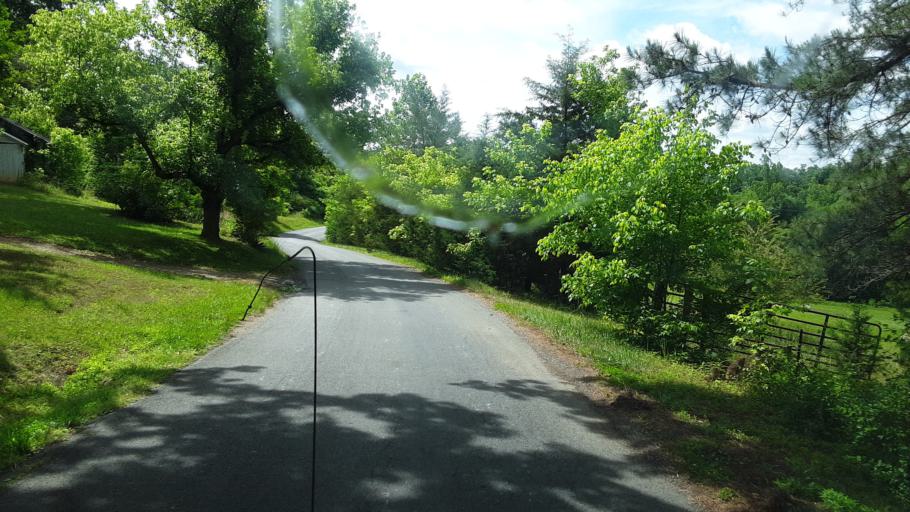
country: US
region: Virginia
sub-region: Pittsylvania County
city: Chatham
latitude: 36.8507
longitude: -79.4522
